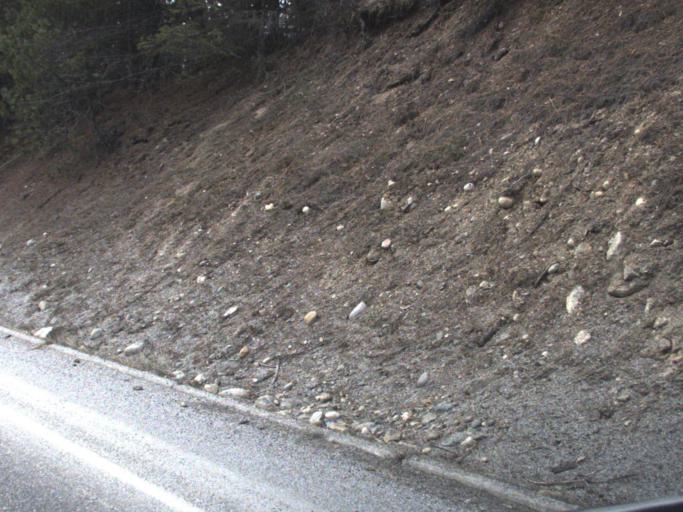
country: US
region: Washington
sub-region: Pend Oreille County
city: Newport
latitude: 48.5300
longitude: -117.3055
